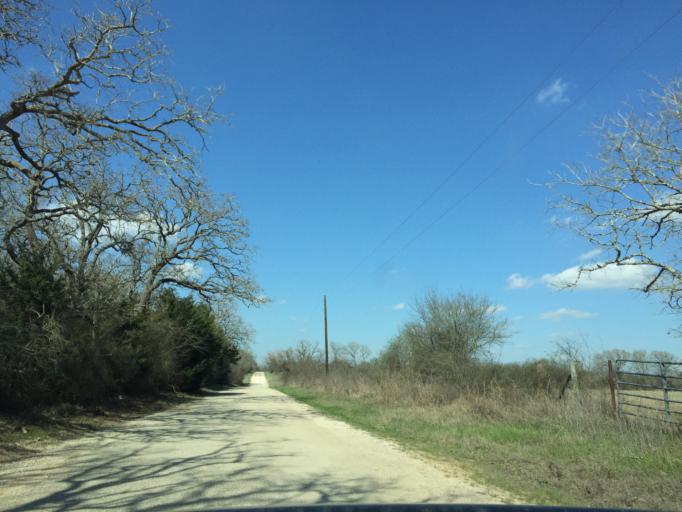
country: US
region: Texas
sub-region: Milam County
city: Thorndale
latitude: 30.5548
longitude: -97.1457
